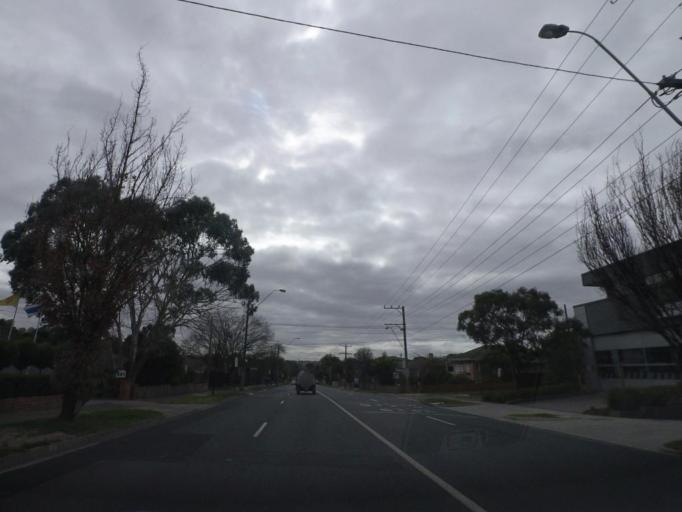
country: AU
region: Victoria
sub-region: Whitehorse
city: Box Hill
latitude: -37.8130
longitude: 145.1157
